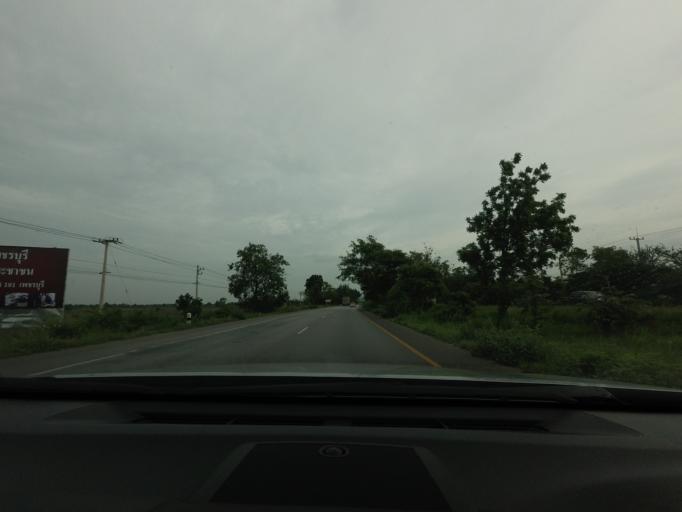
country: TH
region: Phetchaburi
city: Cha-am
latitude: 12.7304
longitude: 99.9273
